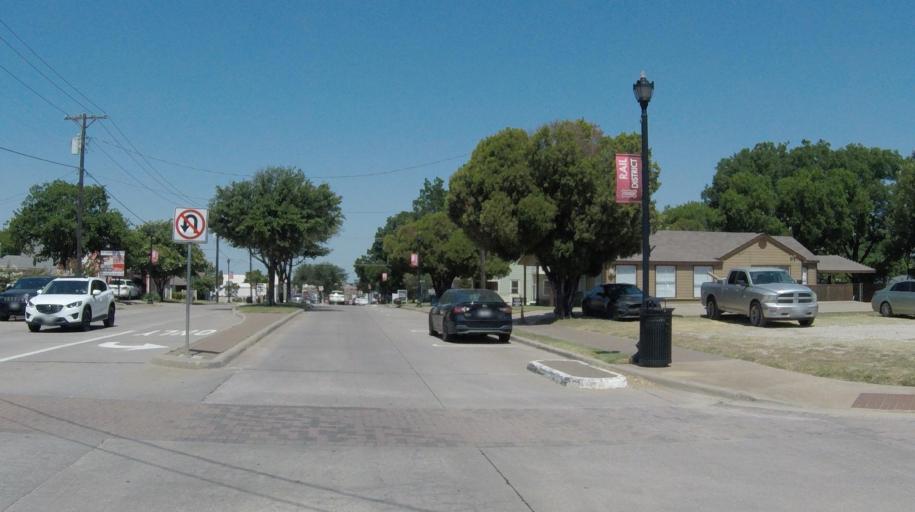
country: US
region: Texas
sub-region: Collin County
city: Frisco
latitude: 33.1501
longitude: -96.8216
